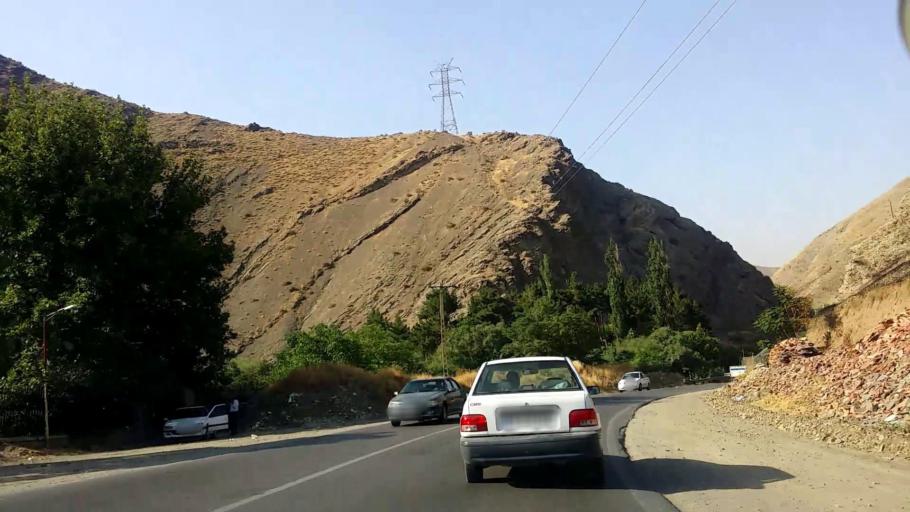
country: IR
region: Alborz
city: Karaj
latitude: 35.8514
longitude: 51.0606
